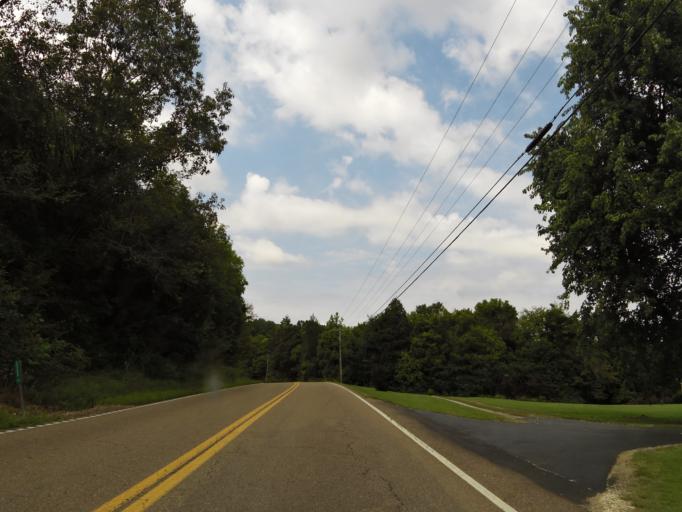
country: US
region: Tennessee
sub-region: Decatur County
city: Decaturville
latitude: 35.5815
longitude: -88.0694
